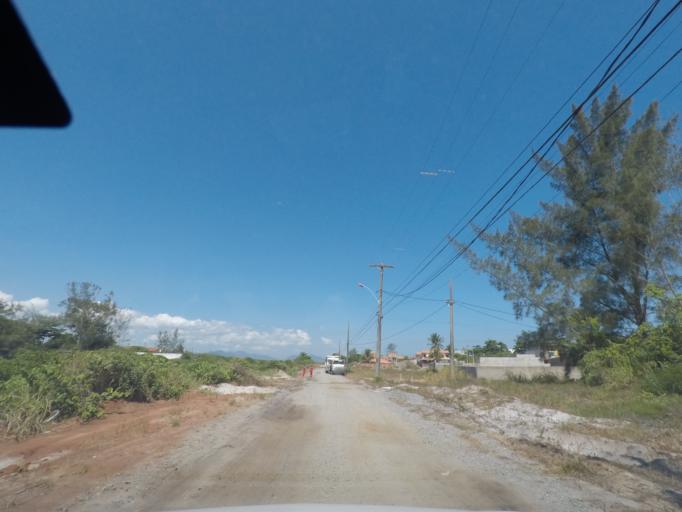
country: BR
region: Rio de Janeiro
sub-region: Marica
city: Marica
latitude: -22.9702
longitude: -42.9077
